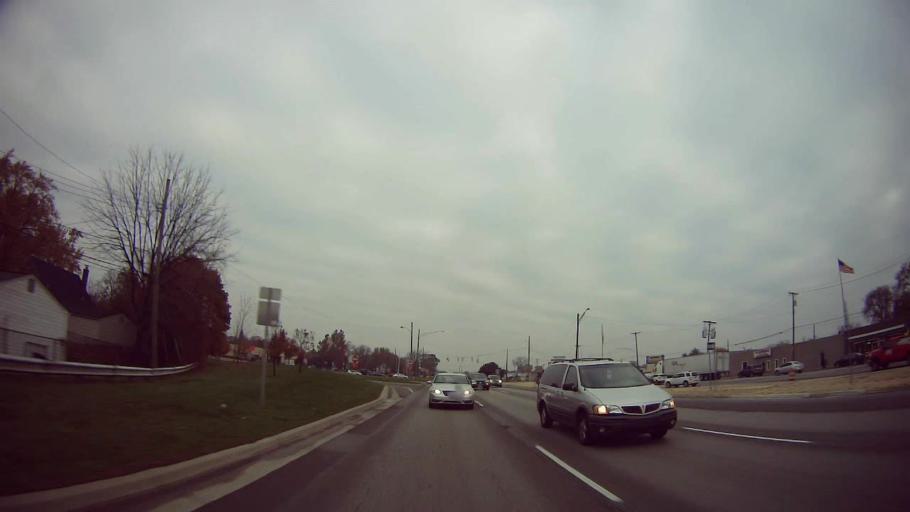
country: US
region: Michigan
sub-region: Wayne County
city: Dearborn Heights
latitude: 42.3259
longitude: -83.2729
